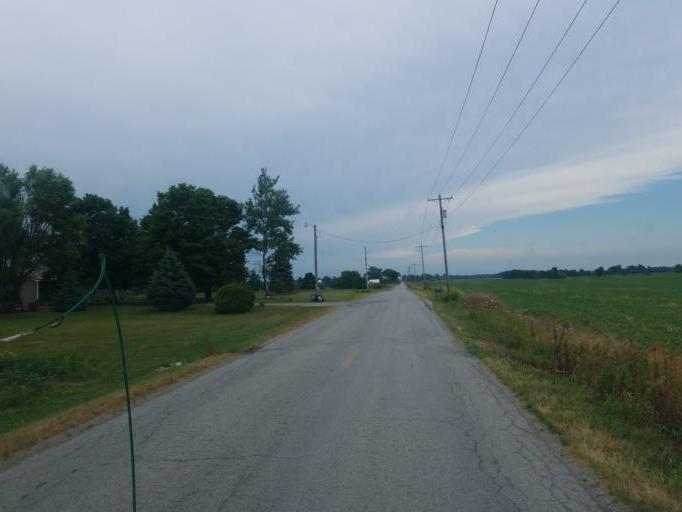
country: US
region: Indiana
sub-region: DeKalb County
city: Butler
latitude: 41.3841
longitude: -84.8889
